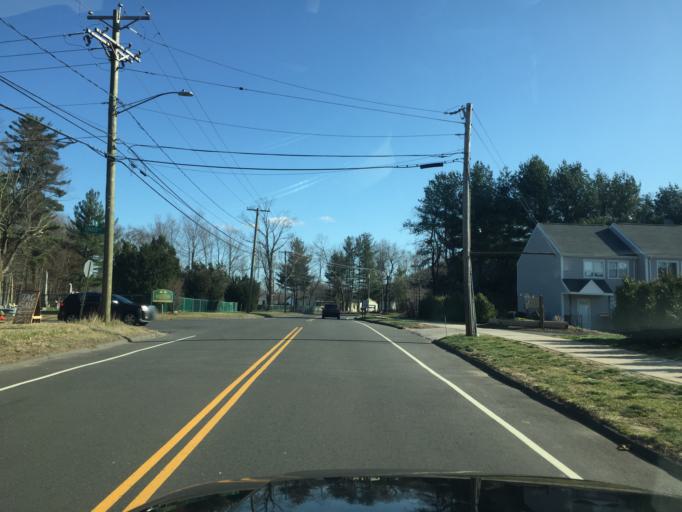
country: US
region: Connecticut
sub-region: Hartford County
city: Bristol
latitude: 41.6530
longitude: -72.9232
